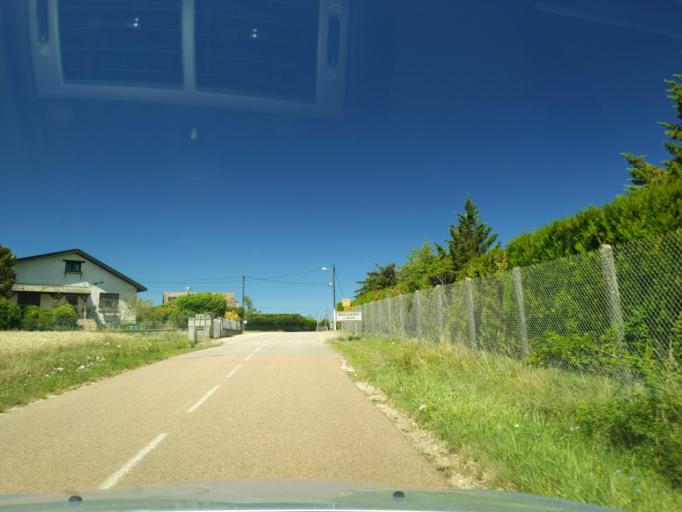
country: FR
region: Bourgogne
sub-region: Departement de la Cote-d'Or
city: Saint-Julien
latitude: 47.4367
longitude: 5.1012
